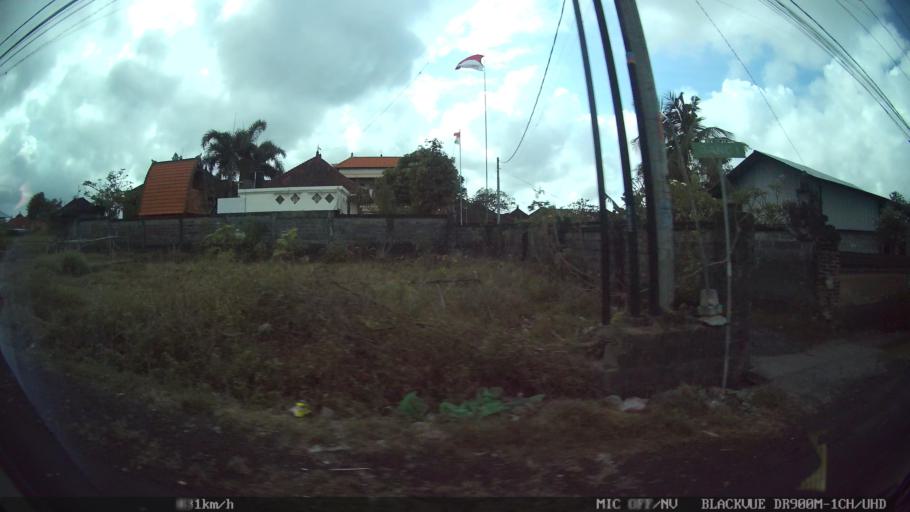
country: ID
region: Bali
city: Banjar Batur
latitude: -8.5975
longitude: 115.2062
